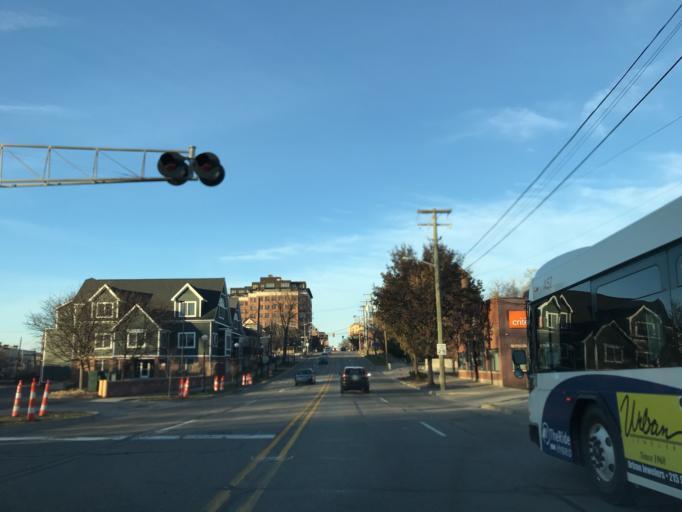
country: US
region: Michigan
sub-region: Washtenaw County
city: Ann Arbor
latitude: 42.2747
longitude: -83.7489
